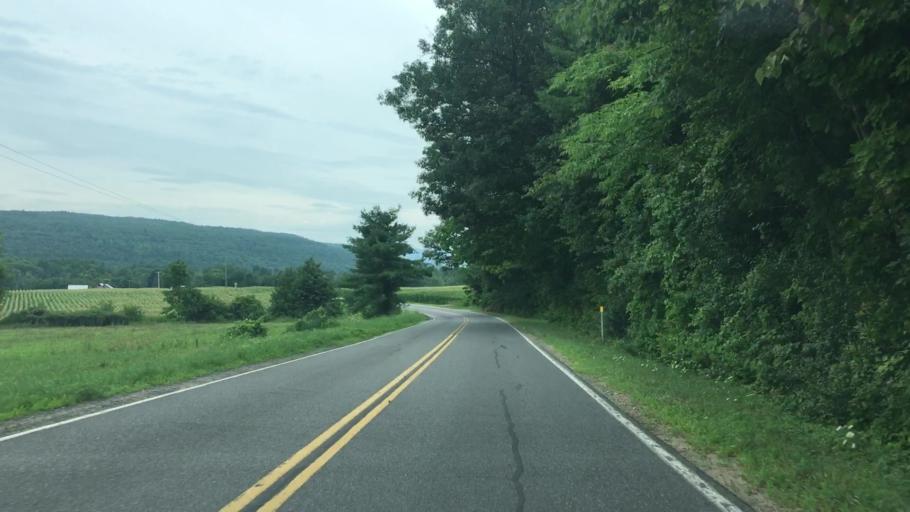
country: US
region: New York
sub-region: Clinton County
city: Peru
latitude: 44.5349
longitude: -73.5735
